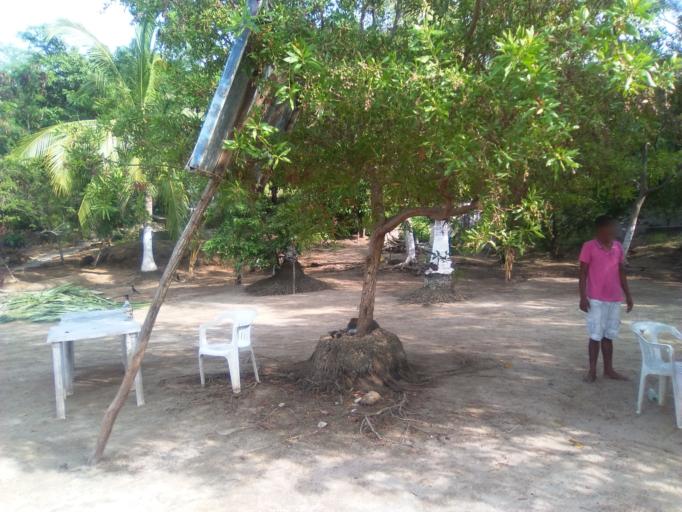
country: MX
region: Guerrero
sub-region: Coyuca de Benitez
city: El Embarcadero
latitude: 16.9559
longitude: -100.0370
